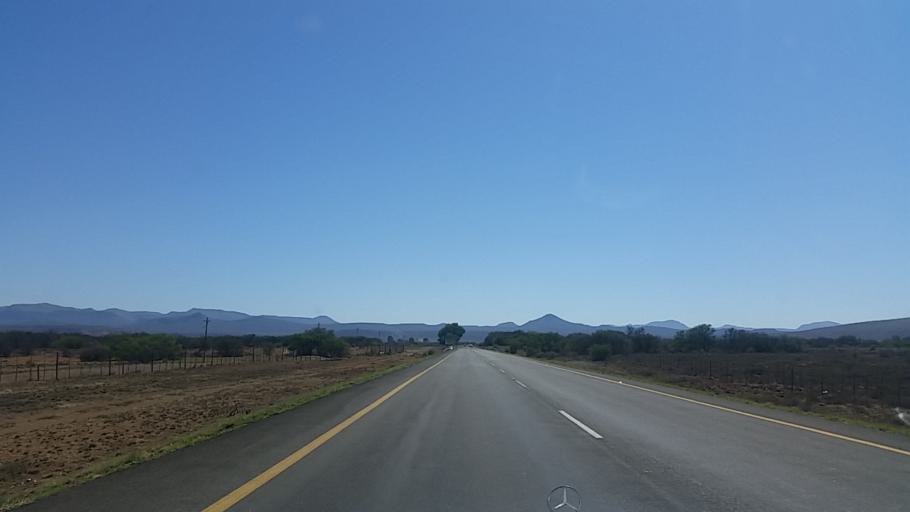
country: ZA
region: Eastern Cape
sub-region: Cacadu District Municipality
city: Graaff-Reinet
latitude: -32.2135
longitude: 24.5457
